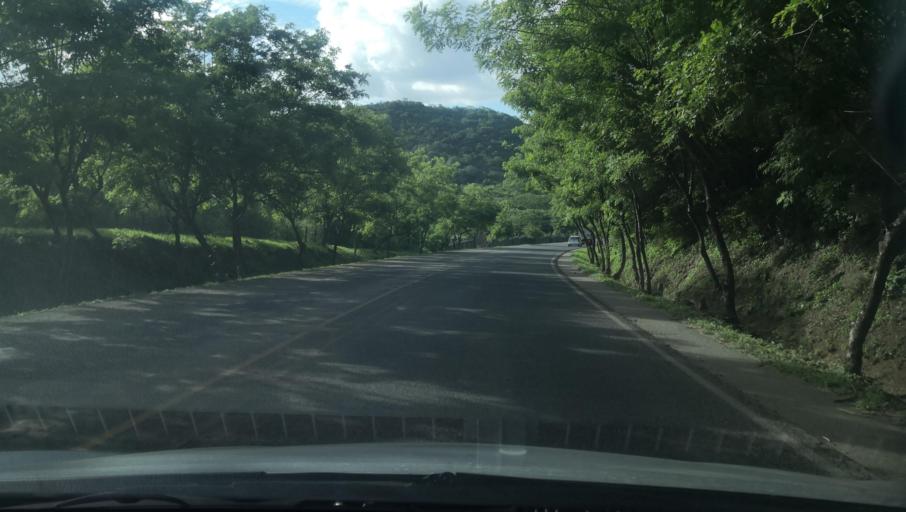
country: NI
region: Madriz
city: Totogalpa
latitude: 13.5821
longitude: -86.4781
